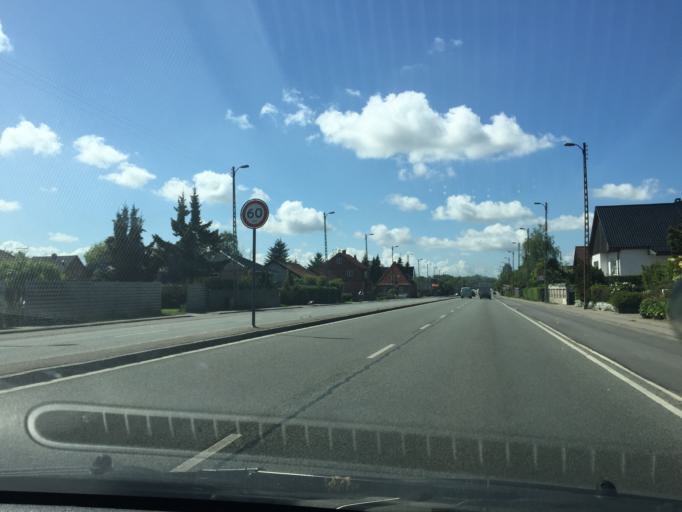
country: DK
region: Capital Region
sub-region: Rodovre Kommune
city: Rodovre
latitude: 55.6920
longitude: 12.4561
